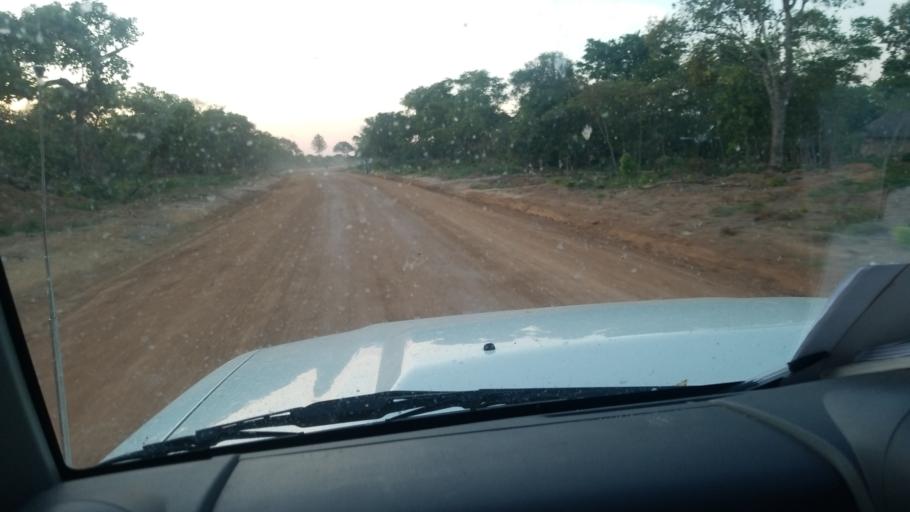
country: ZM
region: Northern
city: Luwingu
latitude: -10.5604
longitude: 29.9964
